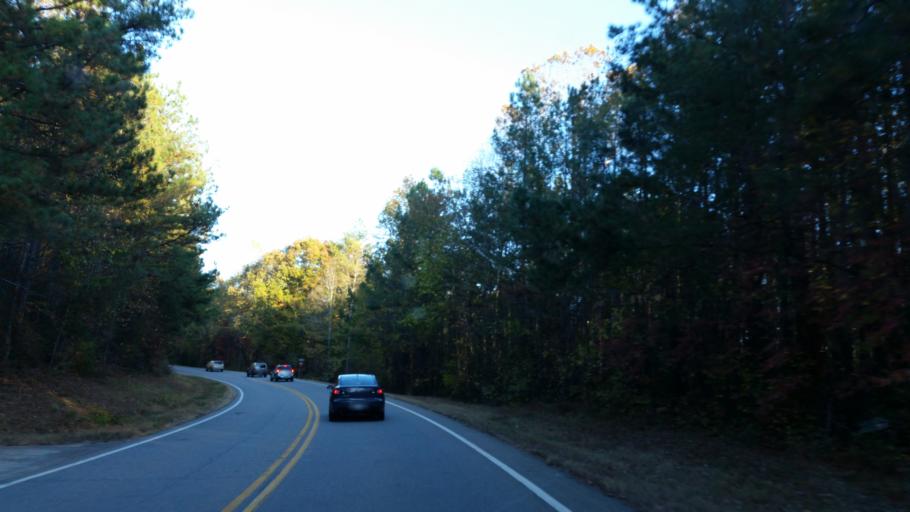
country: US
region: Georgia
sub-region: Dawson County
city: Dawsonville
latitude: 34.5337
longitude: -84.2041
